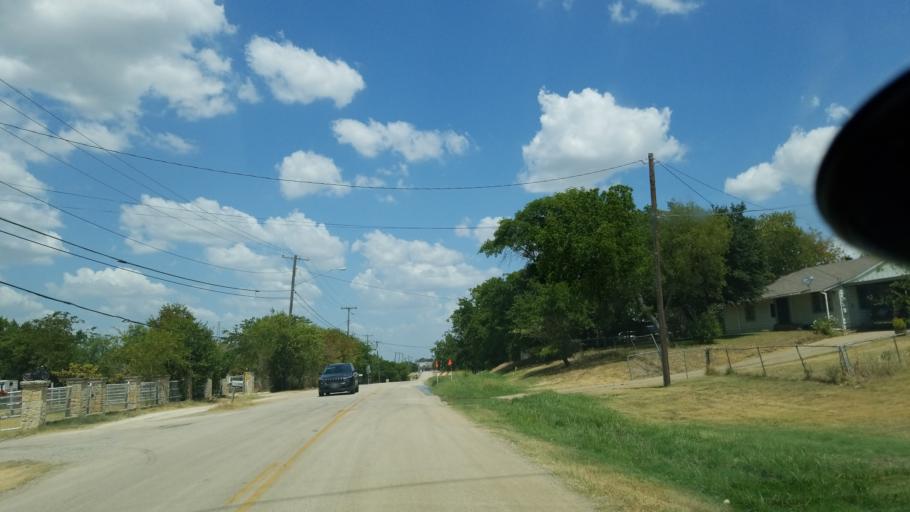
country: US
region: Texas
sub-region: Dallas County
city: Cockrell Hill
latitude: 32.7422
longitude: -96.9274
